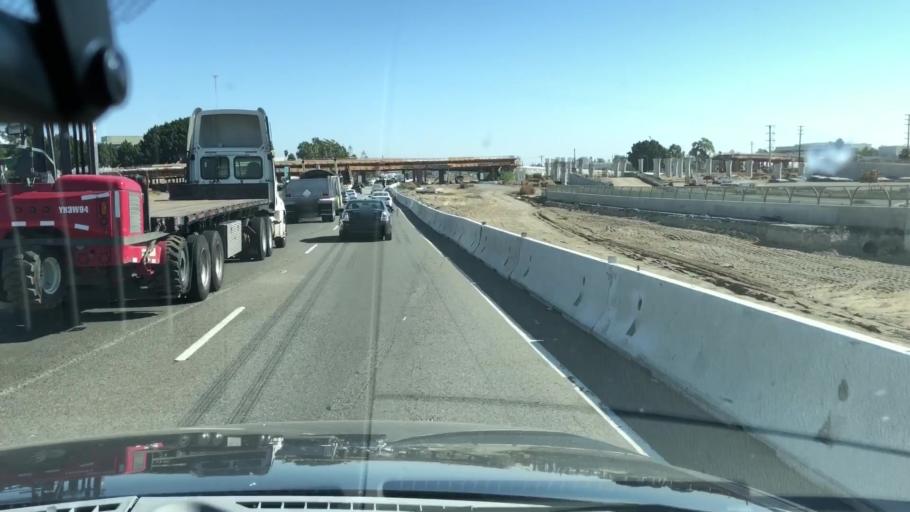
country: US
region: California
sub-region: Los Angeles County
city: La Mirada
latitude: 33.8857
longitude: -118.0318
